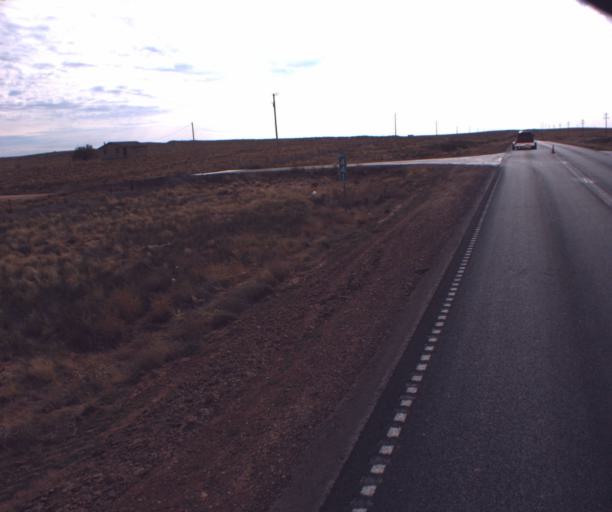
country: US
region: Arizona
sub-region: Apache County
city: Chinle
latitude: 36.0838
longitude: -109.6186
